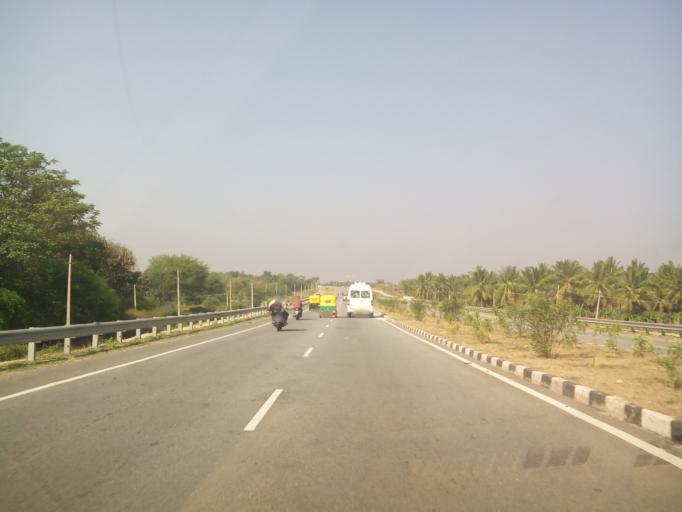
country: IN
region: Karnataka
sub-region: Tumkur
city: Kunigal
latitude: 13.0204
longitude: 77.0519
